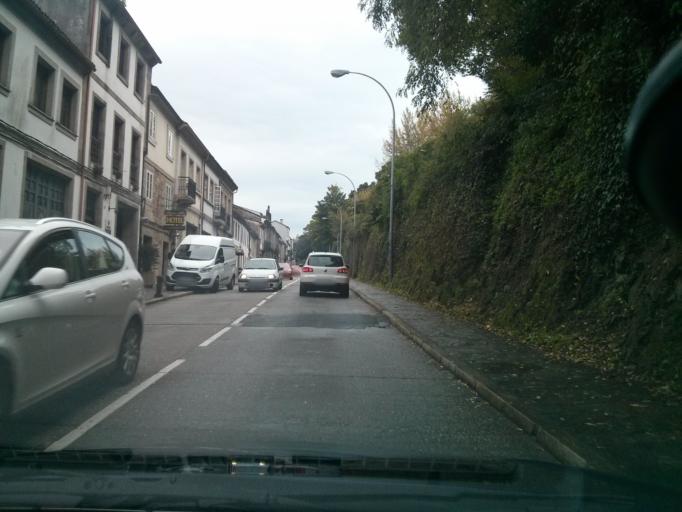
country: ES
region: Galicia
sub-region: Provincia da Coruna
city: Santiago de Compostela
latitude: 42.8796
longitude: -8.5492
